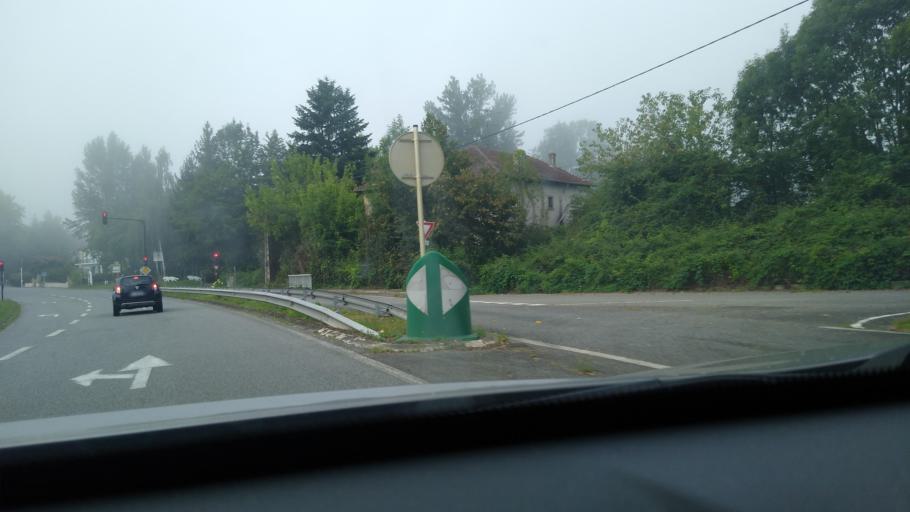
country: FR
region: Midi-Pyrenees
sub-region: Departement de la Haute-Garonne
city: Salies-du-Salat
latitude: 43.0918
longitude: 0.9500
